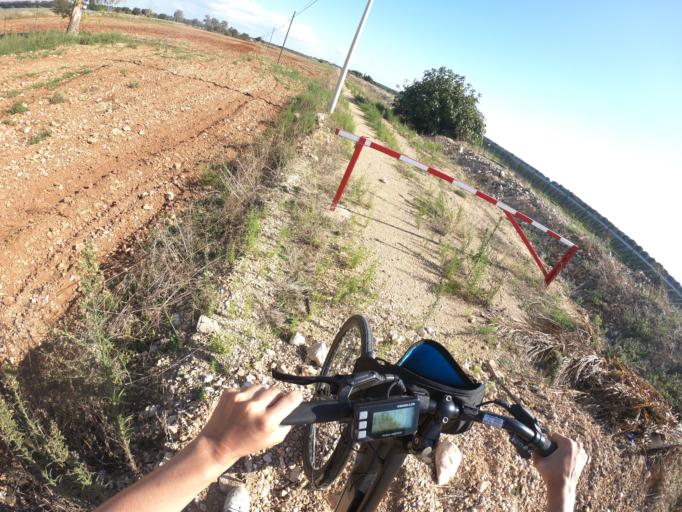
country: IT
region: Apulia
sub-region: Provincia di Lecce
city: Leverano
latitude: 40.2190
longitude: 17.9761
